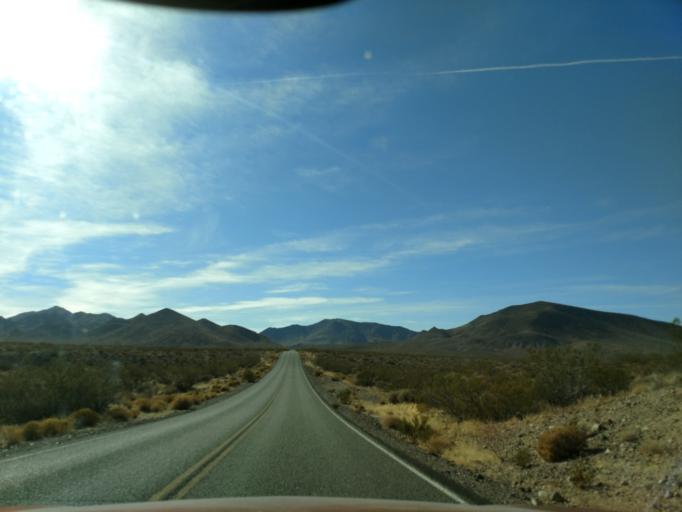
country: US
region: Nevada
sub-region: Nye County
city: Beatty
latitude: 36.8205
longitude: -116.8954
